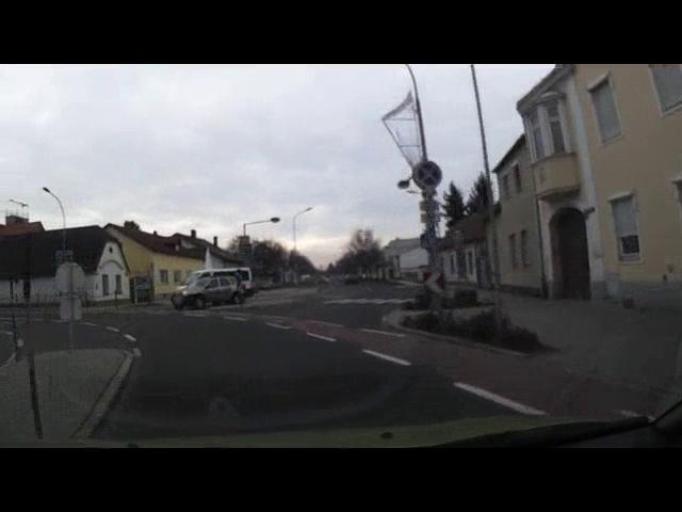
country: AT
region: Burgenland
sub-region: Eisenstadt-Umgebung
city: Neufeld an der Leitha
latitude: 47.8658
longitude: 16.3768
